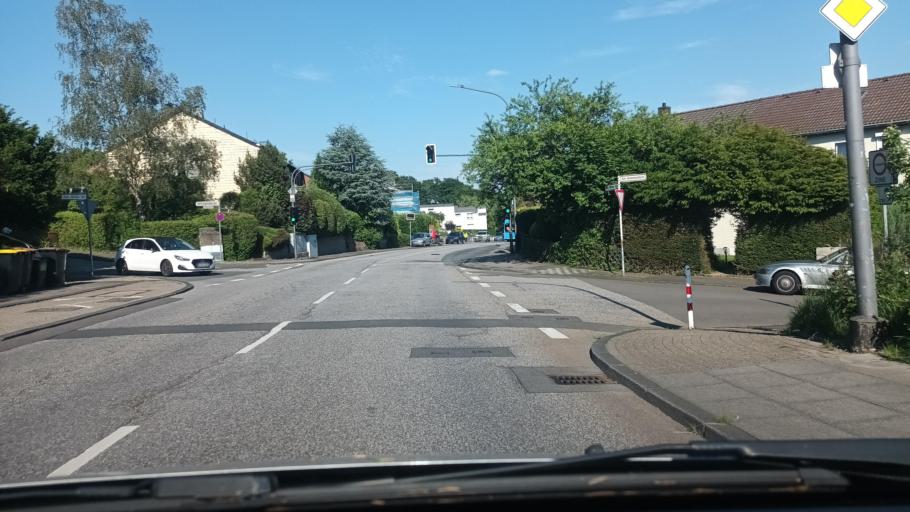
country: DE
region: North Rhine-Westphalia
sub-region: Regierungsbezirk Dusseldorf
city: Wuppertal
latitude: 51.2856
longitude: 7.1621
